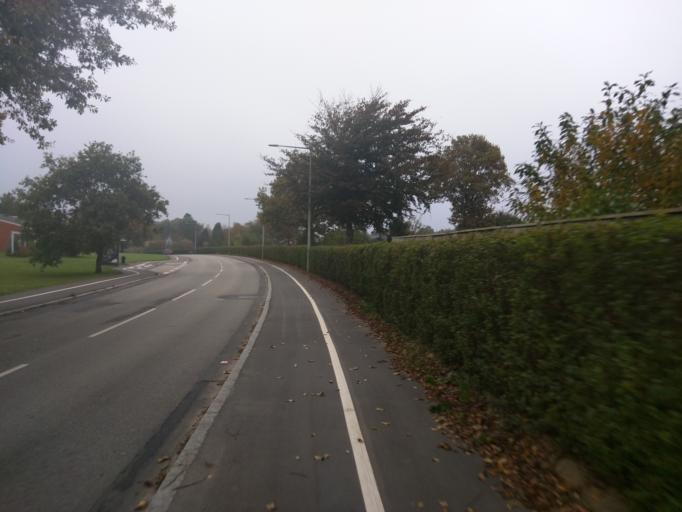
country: DK
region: Central Jutland
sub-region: Silkeborg Kommune
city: Silkeborg
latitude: 56.1924
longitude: 9.5243
